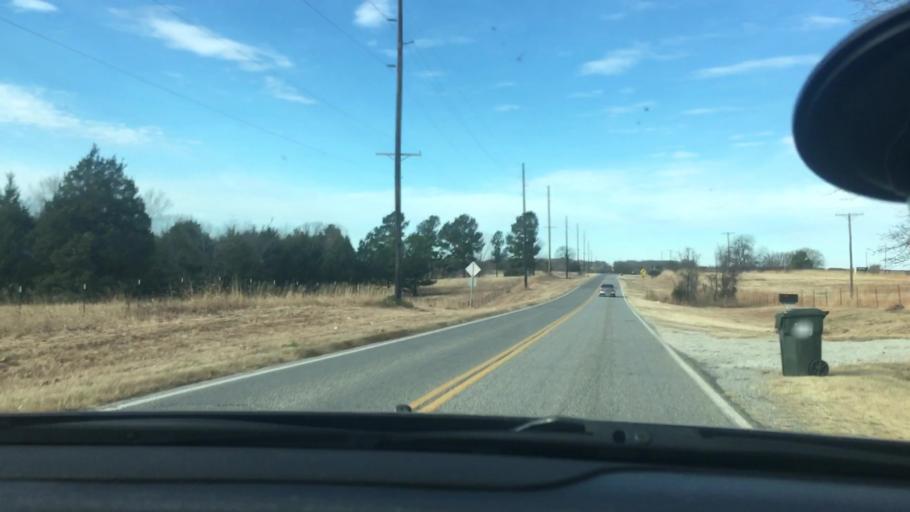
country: US
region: Oklahoma
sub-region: Seminole County
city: Konawa
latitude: 34.9417
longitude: -96.7070
